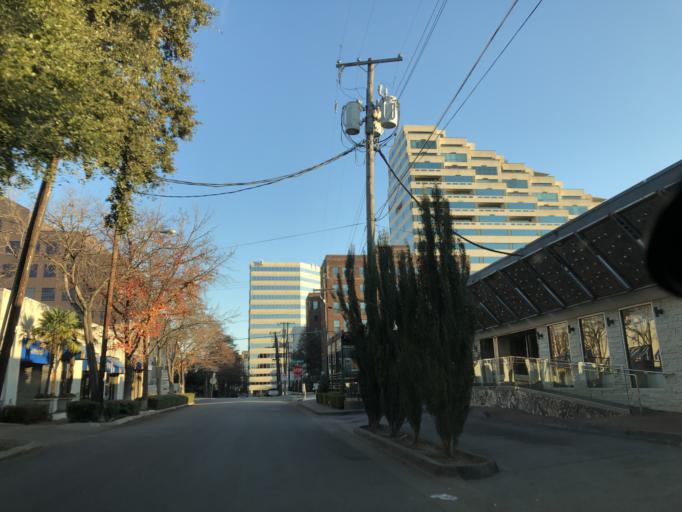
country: US
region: Texas
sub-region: Dallas County
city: Dallas
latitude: 32.8106
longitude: -96.8083
